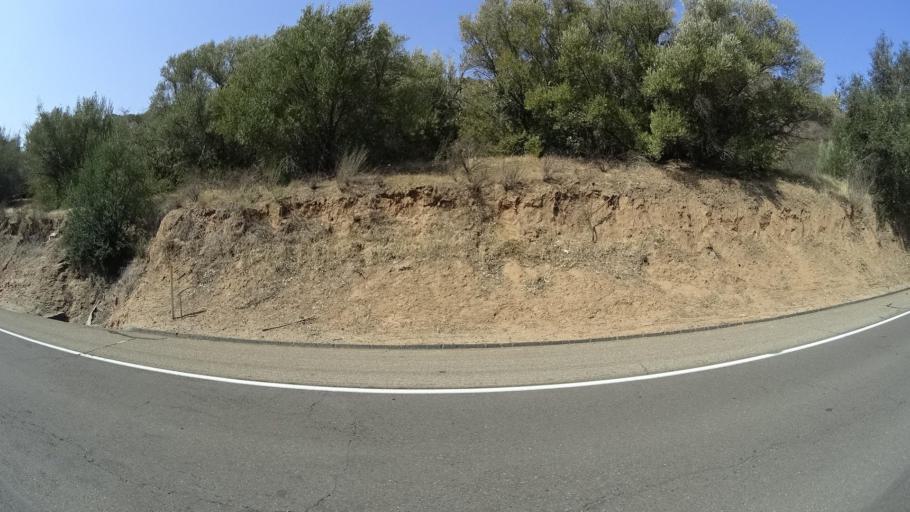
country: US
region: California
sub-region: San Diego County
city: Rainbow
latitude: 33.3668
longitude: -117.1652
